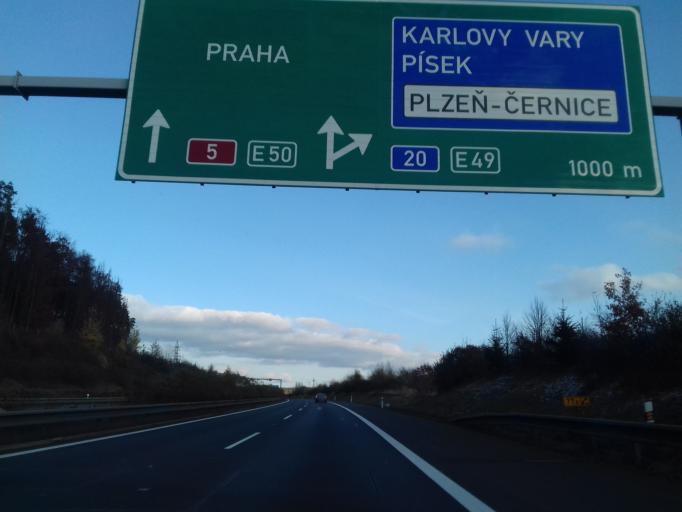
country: CZ
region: Plzensky
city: Stenovice
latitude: 49.6811
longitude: 13.4143
